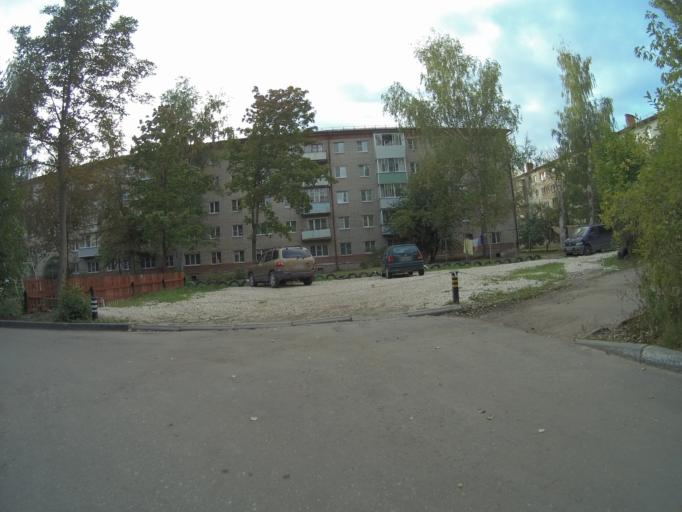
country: RU
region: Vladimir
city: Raduzhnyy
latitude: 56.1059
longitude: 40.2844
